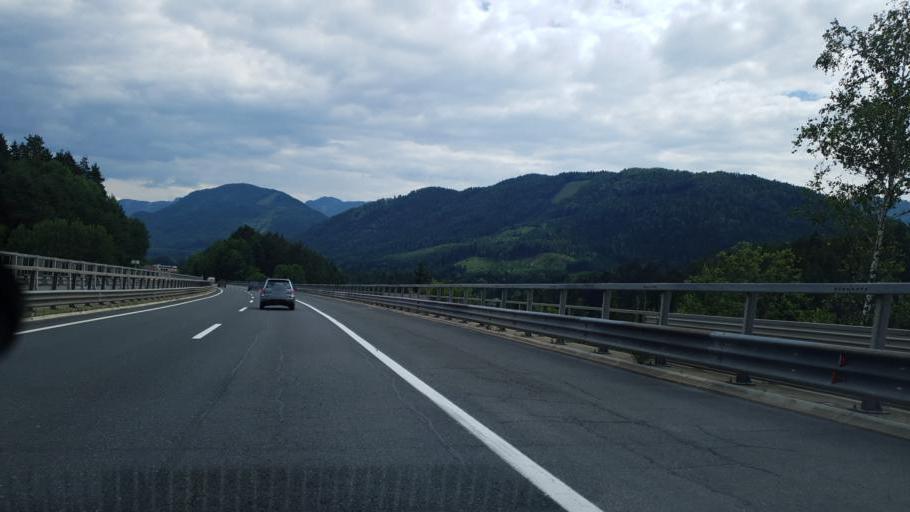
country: AT
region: Carinthia
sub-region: Politischer Bezirk Villach Land
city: Paternion
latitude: 46.7036
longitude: 13.6372
